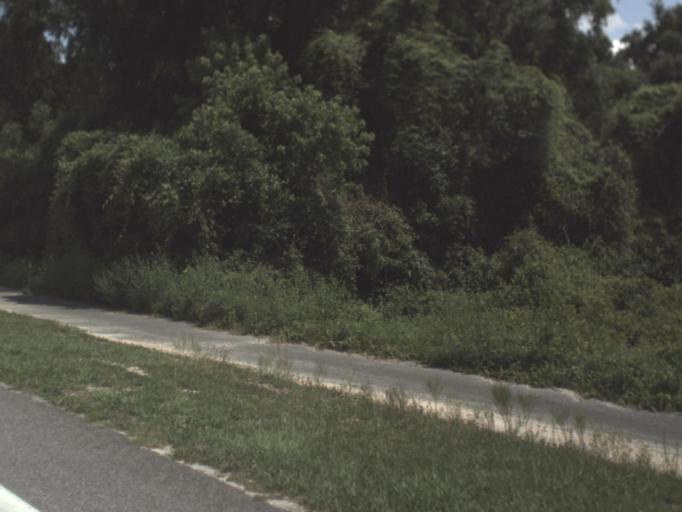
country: US
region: Florida
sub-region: Alachua County
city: High Springs
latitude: 29.9293
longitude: -82.7245
